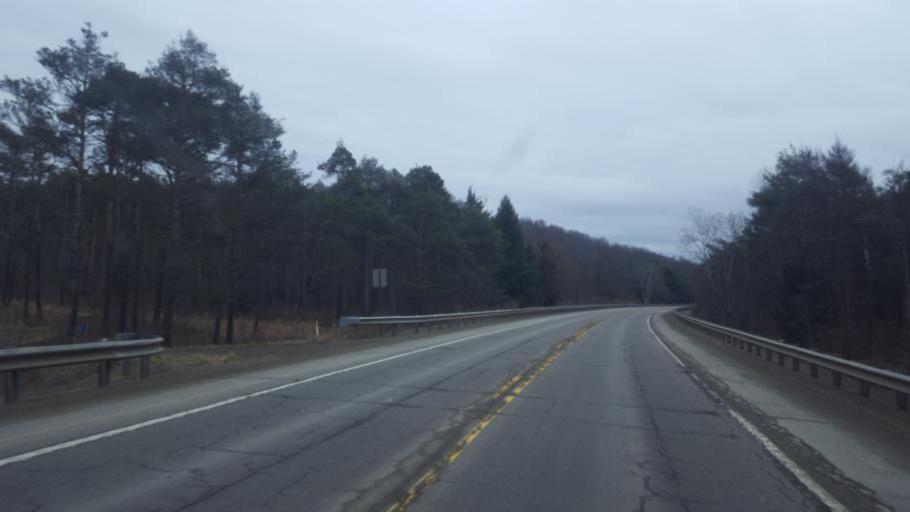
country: US
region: Pennsylvania
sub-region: Potter County
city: Coudersport
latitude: 41.7818
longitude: -78.1506
